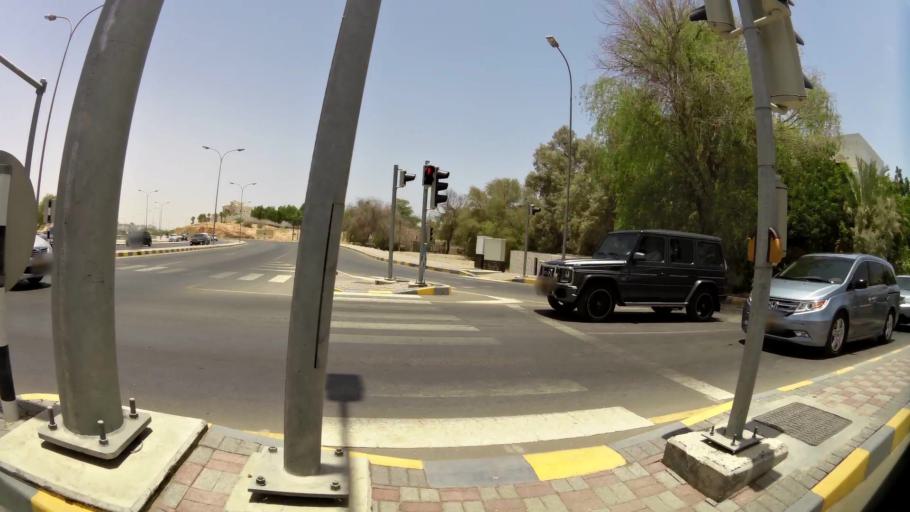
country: OM
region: Muhafazat Masqat
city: Bawshar
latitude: 23.5980
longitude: 58.4554
